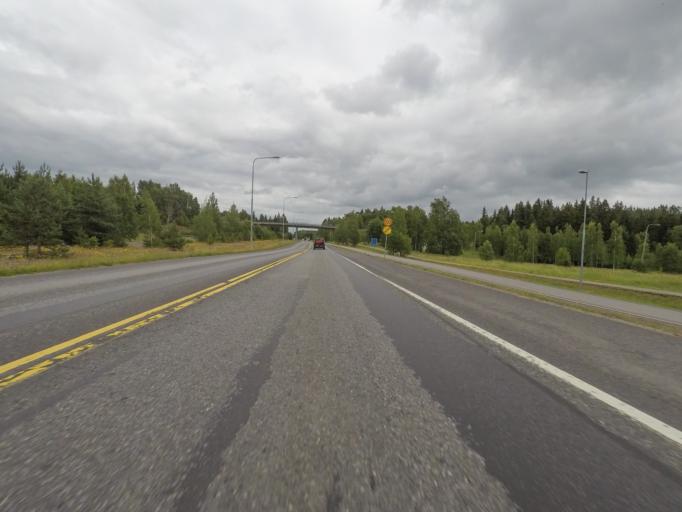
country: FI
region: Varsinais-Suomi
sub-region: Turku
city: Kaarina
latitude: 60.4709
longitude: 22.3641
